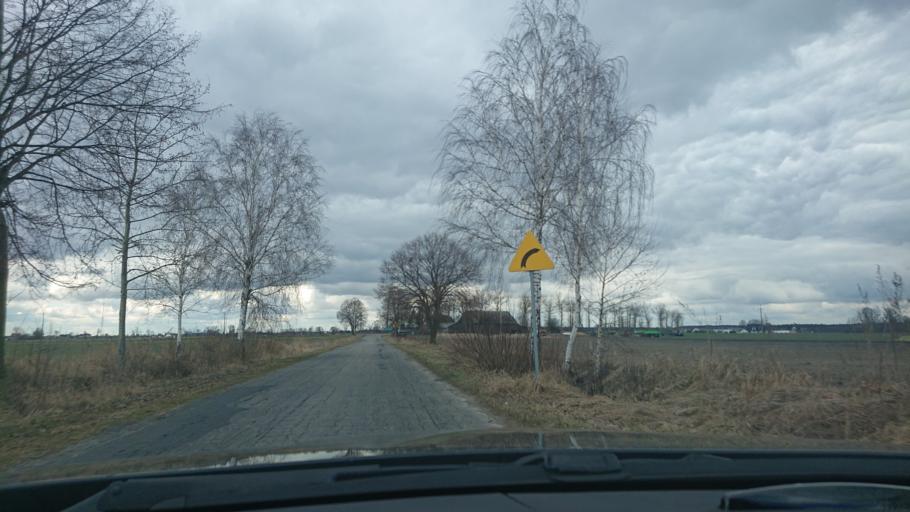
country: PL
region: Greater Poland Voivodeship
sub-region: Powiat gnieznienski
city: Trzemeszno
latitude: 52.5838
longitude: 17.7049
